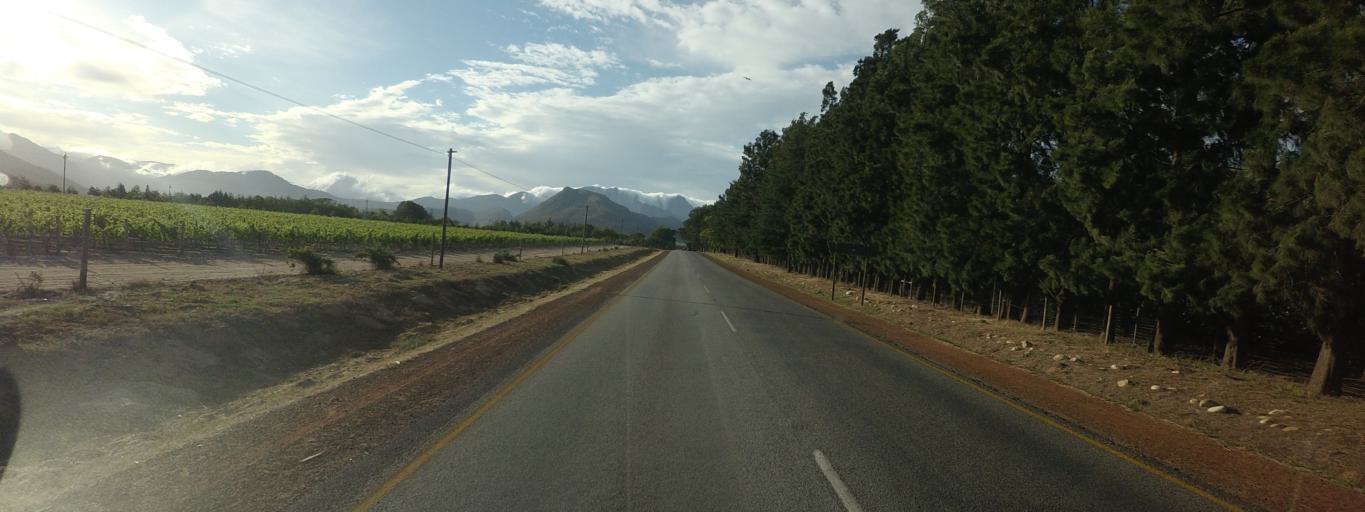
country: ZA
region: Western Cape
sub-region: Cape Winelands District Municipality
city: Paarl
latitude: -33.8671
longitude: 19.0415
